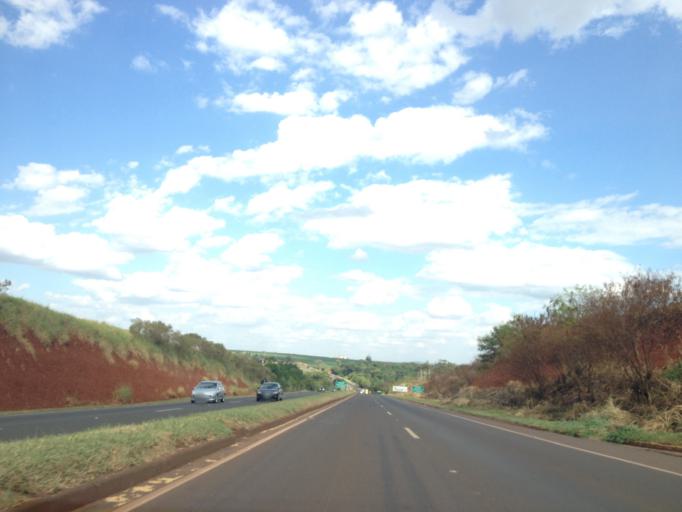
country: BR
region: Parana
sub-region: Marialva
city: Marialva
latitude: -23.4827
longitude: -51.8221
